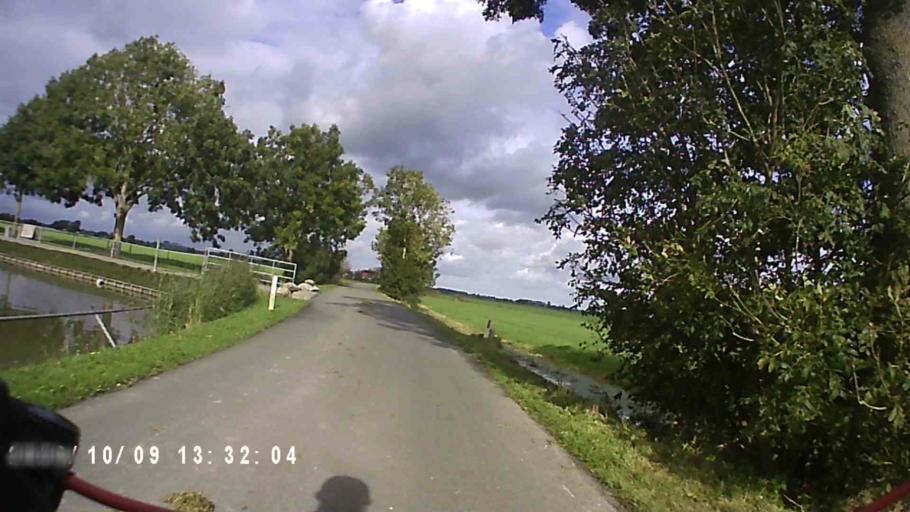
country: NL
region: Groningen
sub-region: Gemeente Zuidhorn
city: Aduard
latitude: 53.2832
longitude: 6.4735
